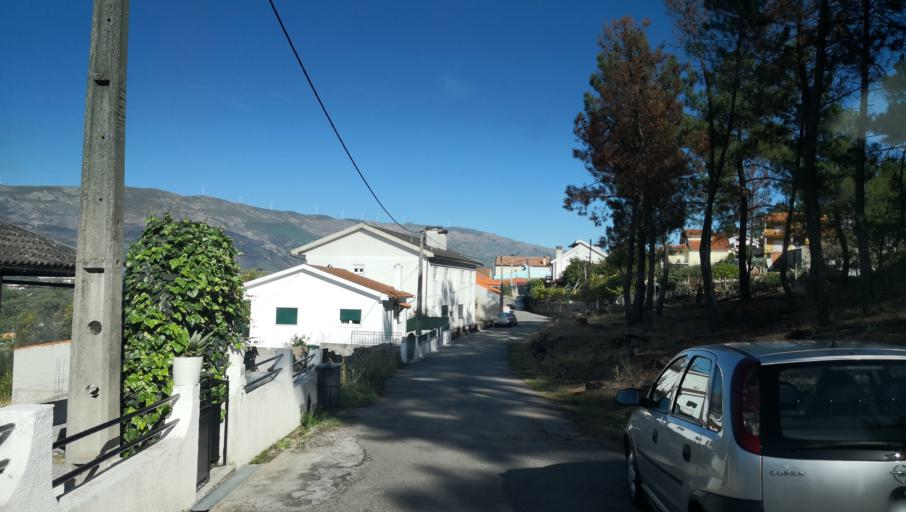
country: PT
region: Vila Real
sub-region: Vila Real
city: Vila Real
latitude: 41.3183
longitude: -7.7096
